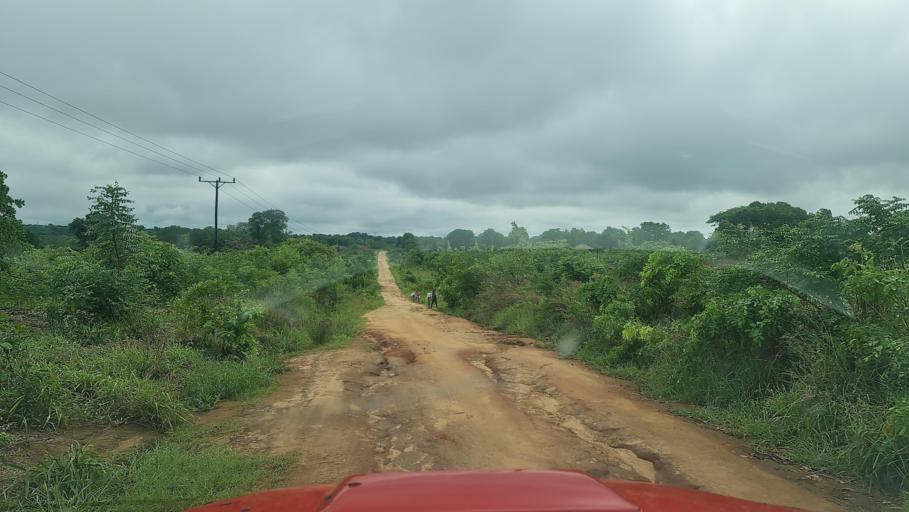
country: MW
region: Southern Region
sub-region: Nsanje District
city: Nsanje
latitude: -17.1910
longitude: 35.8662
